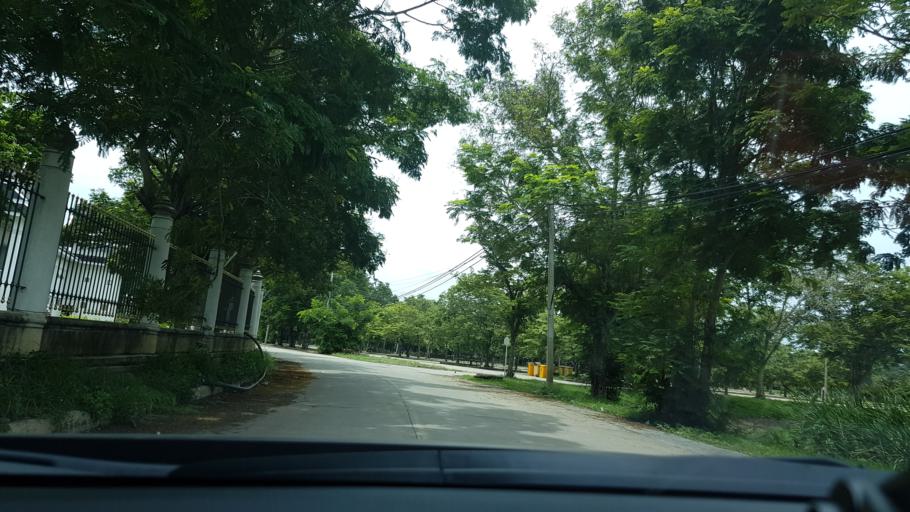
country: TH
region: Pathum Thani
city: Sam Khok
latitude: 14.1497
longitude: 100.5215
